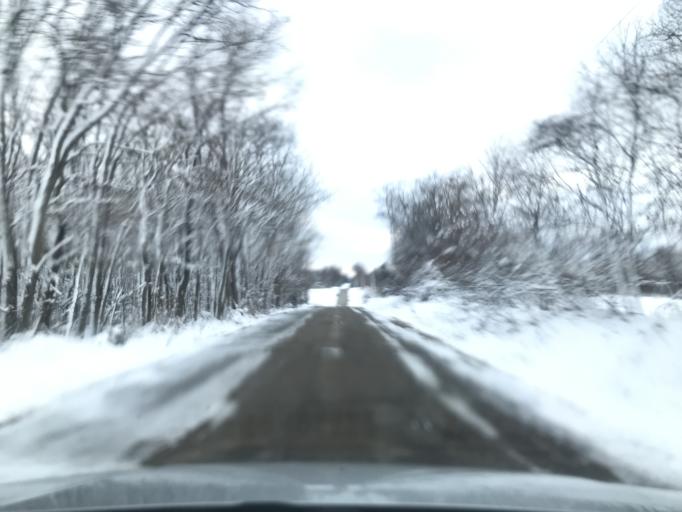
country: US
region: Wisconsin
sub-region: Oconto County
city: Oconto
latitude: 44.9192
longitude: -88.0015
